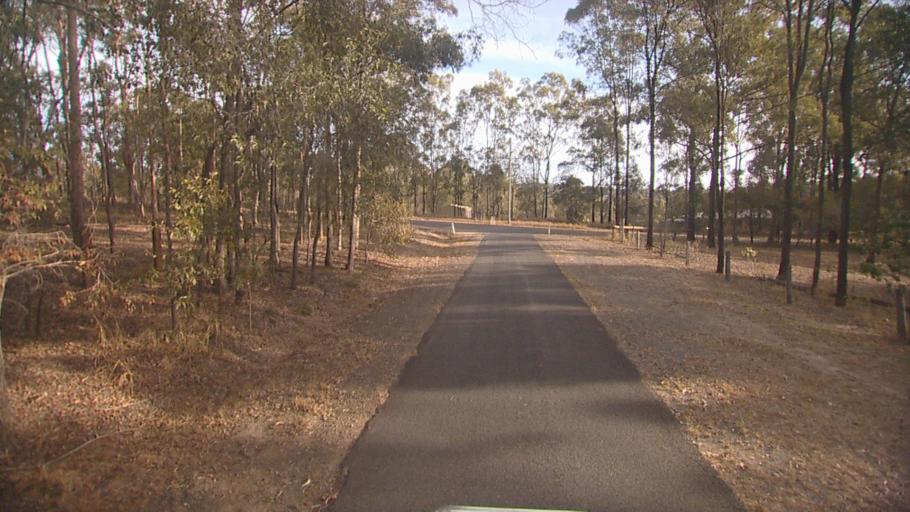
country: AU
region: Queensland
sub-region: Logan
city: Cedar Vale
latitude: -27.8750
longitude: 153.0271
